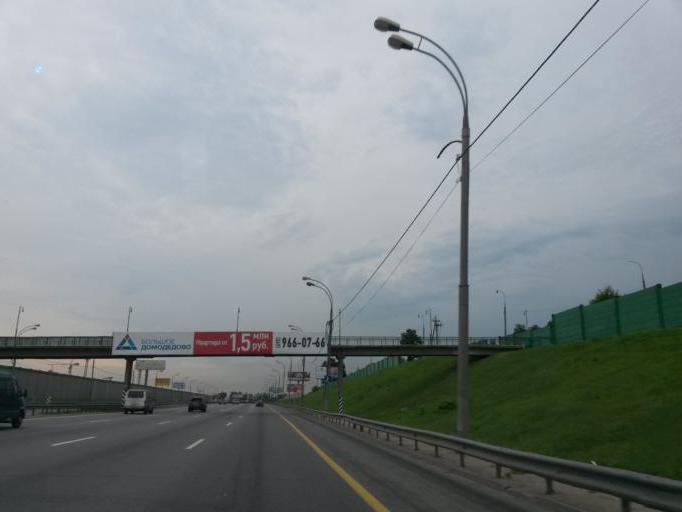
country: RU
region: Moskovskaya
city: Vidnoye
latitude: 55.5598
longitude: 37.6885
